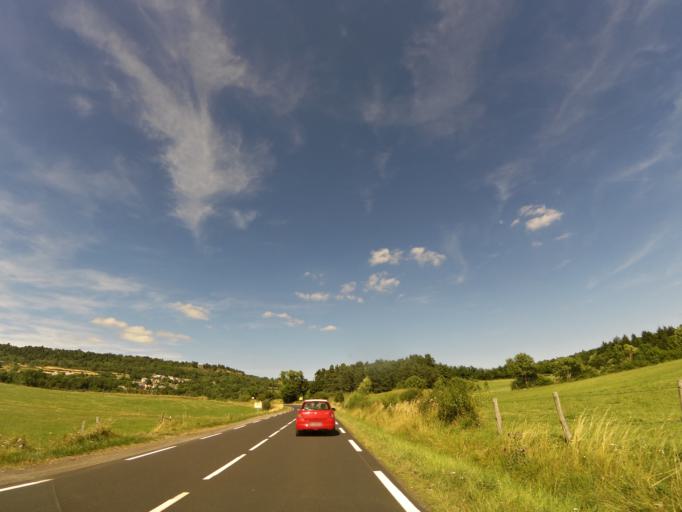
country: FR
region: Auvergne
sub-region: Departement du Puy-de-Dome
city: Aydat
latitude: 45.5856
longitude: 2.9604
